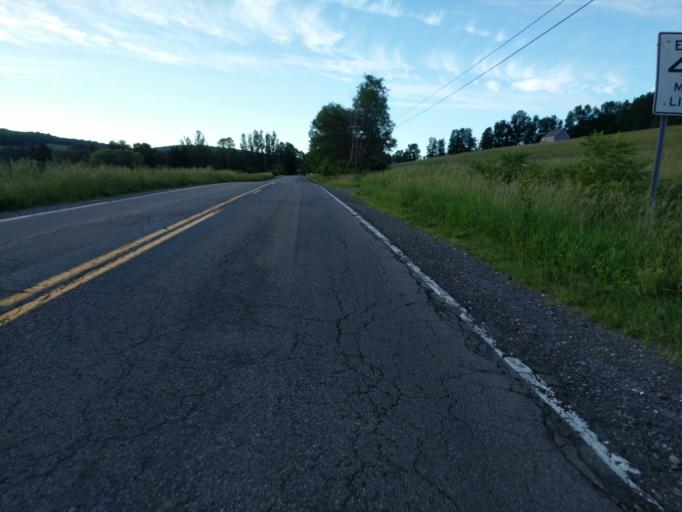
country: US
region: New York
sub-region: Tompkins County
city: Dryden
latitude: 42.4015
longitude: -76.3503
